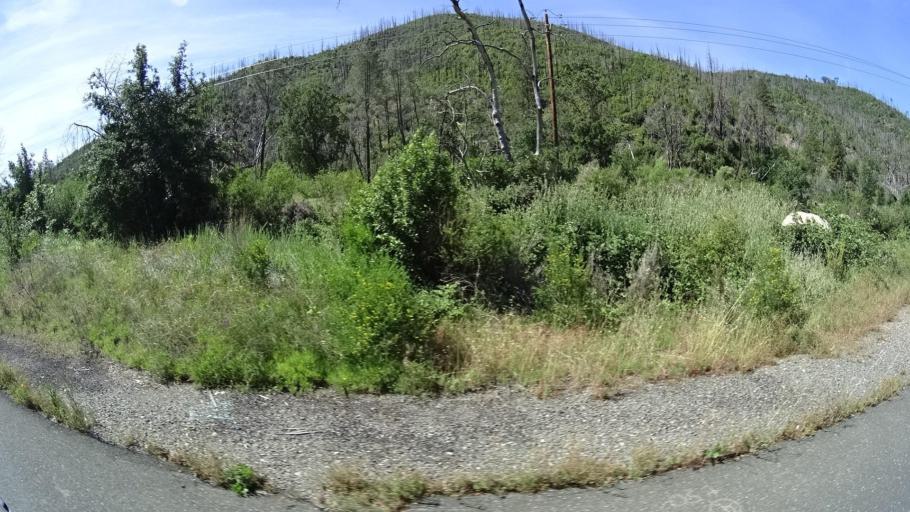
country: US
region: California
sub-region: Lake County
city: Middletown
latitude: 38.7747
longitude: -122.6716
